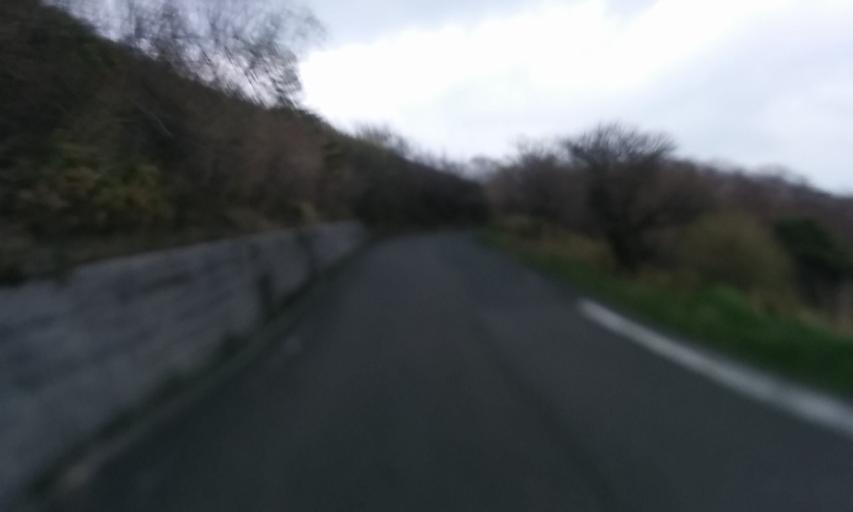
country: JP
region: Ehime
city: Saijo
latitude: 33.7787
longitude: 133.2208
